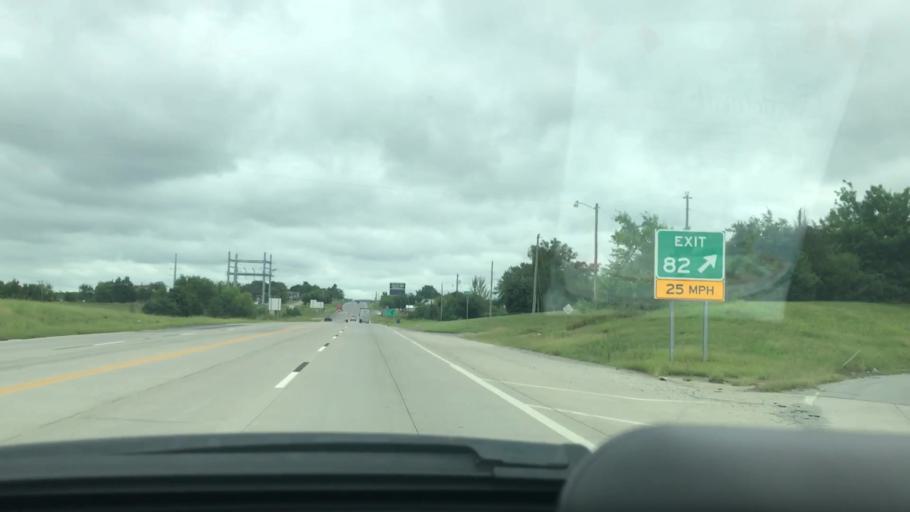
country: US
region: Oklahoma
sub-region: Pittsburg County
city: McAlester
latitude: 34.8367
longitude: -95.8363
